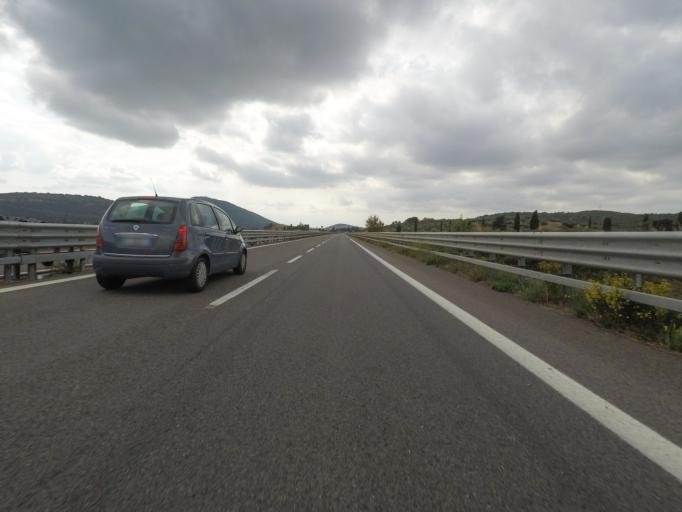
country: IT
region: Tuscany
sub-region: Provincia di Grosseto
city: Bagno Roselle
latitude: 42.8442
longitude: 11.1547
